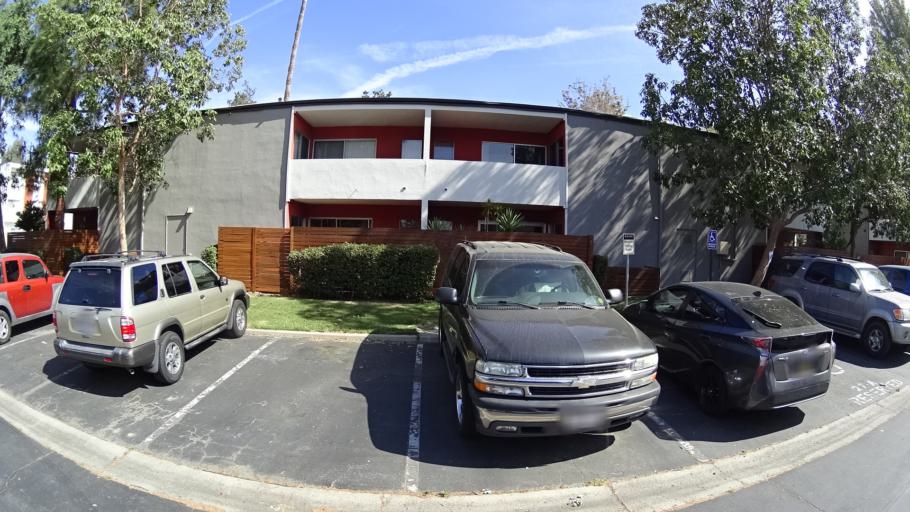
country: US
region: California
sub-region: Ventura County
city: Thousand Oaks
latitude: 34.1836
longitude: -118.8720
